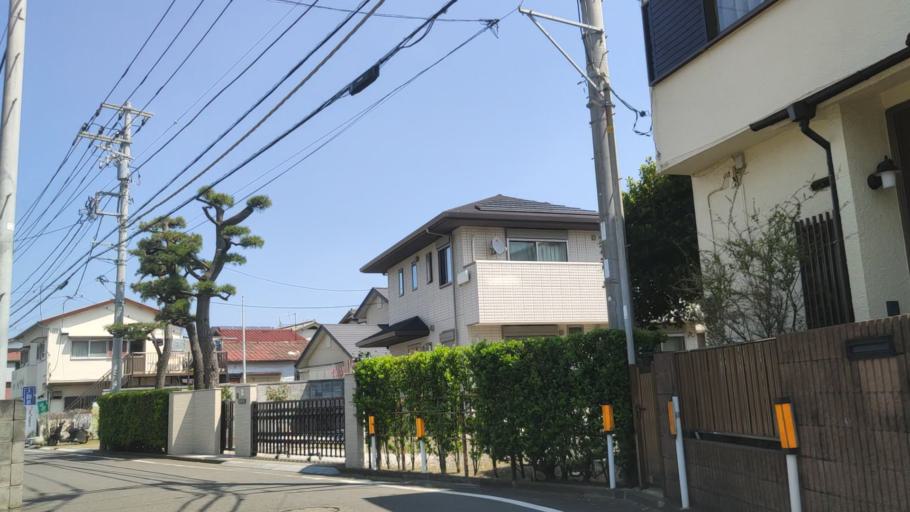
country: JP
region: Kanagawa
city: Oiso
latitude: 35.3128
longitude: 139.3204
